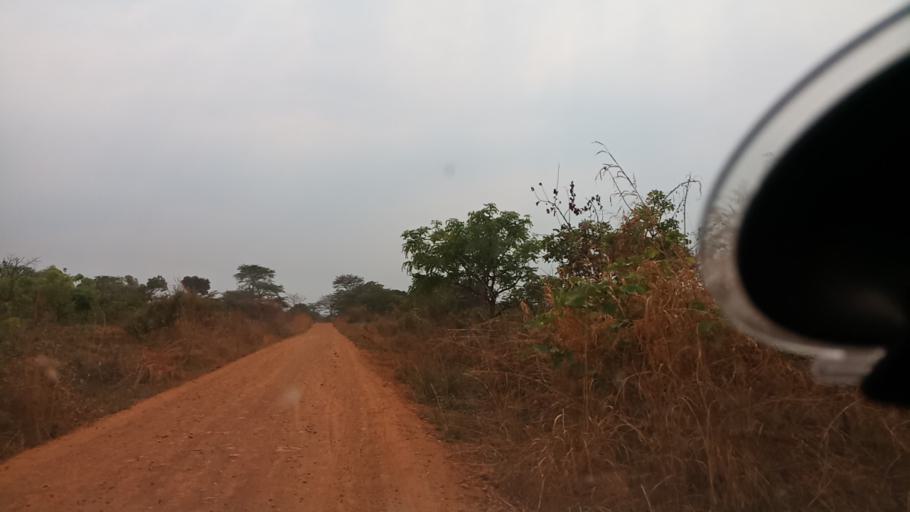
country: ZM
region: Luapula
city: Nchelenge
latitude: -9.0955
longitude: 28.3236
